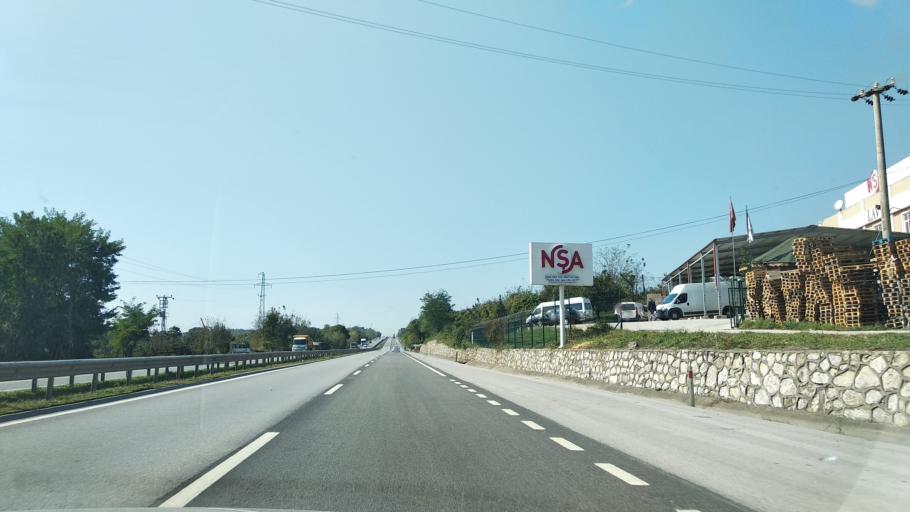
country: TR
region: Kocaeli
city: Derbent
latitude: 40.7318
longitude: 30.1757
